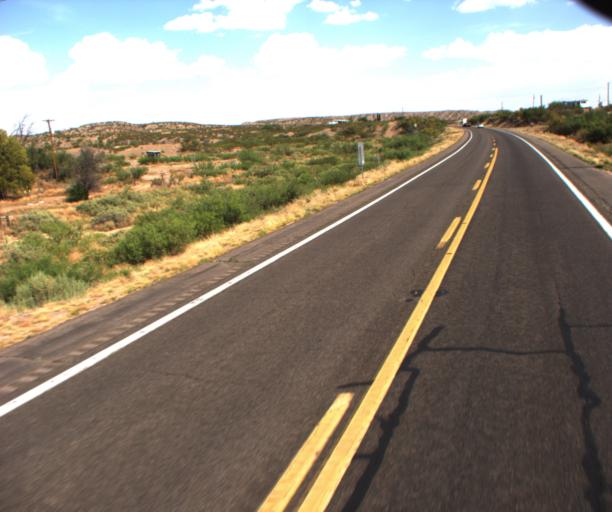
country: US
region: Arizona
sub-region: Greenlee County
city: Clifton
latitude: 32.8170
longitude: -109.1717
